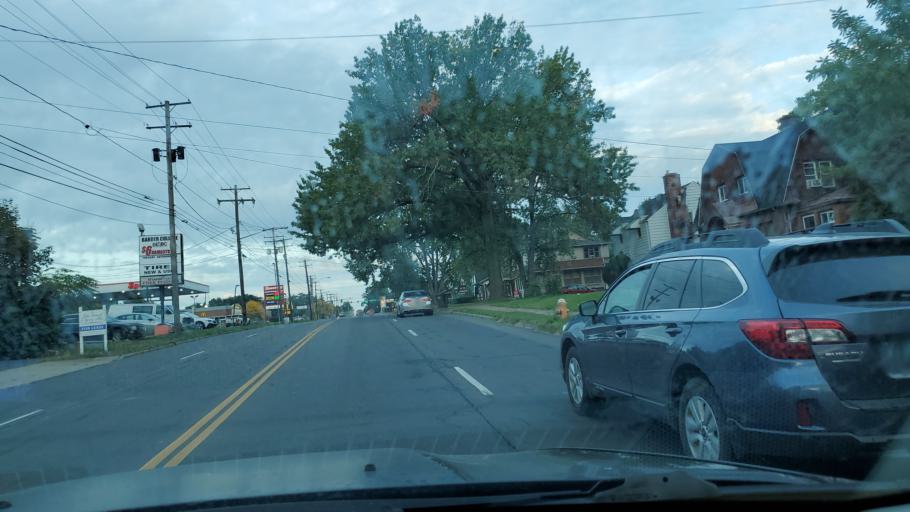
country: US
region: Ohio
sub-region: Mahoning County
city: Struthers
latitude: 41.0608
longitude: -80.6414
